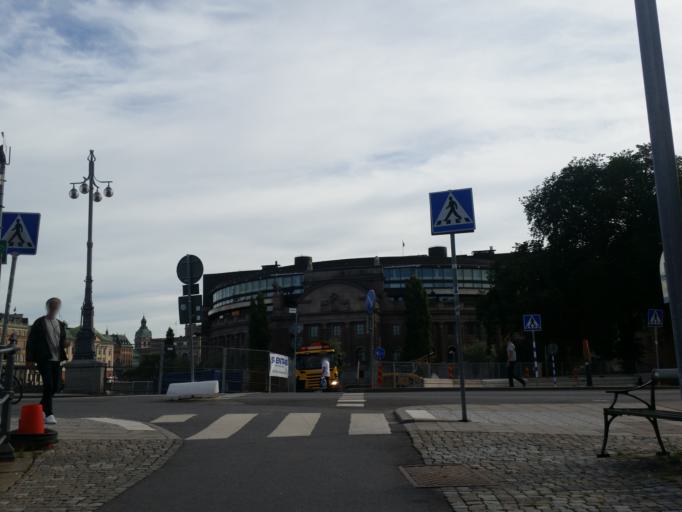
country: SE
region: Stockholm
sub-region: Stockholms Kommun
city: Stockholm
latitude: 59.3265
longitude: 18.0652
